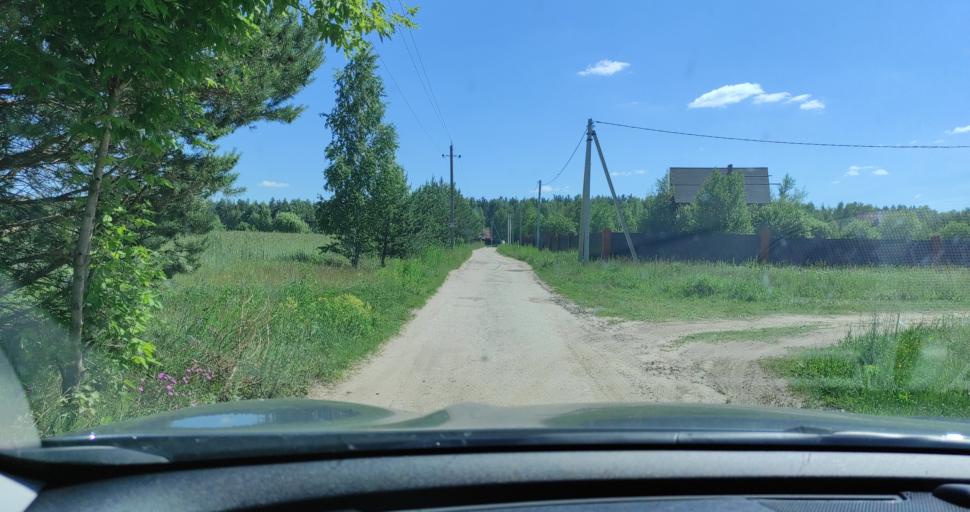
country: RU
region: Rjazan
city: Murmino
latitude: 54.5635
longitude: 40.0976
